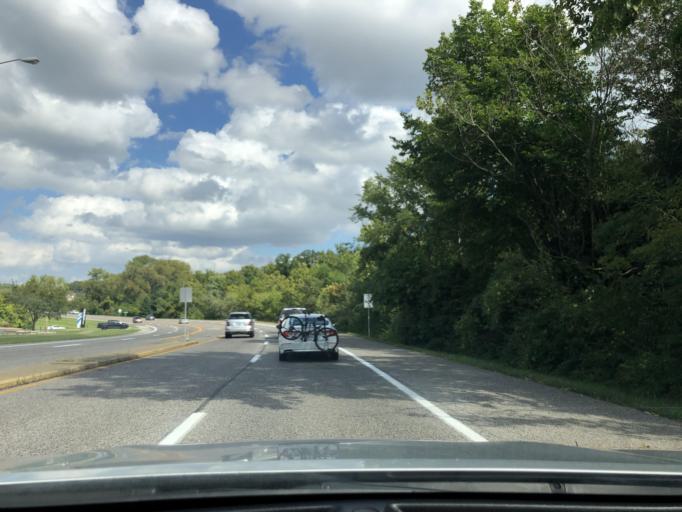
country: US
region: Missouri
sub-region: Saint Louis County
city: Green Park
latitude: 38.5309
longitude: -90.3435
